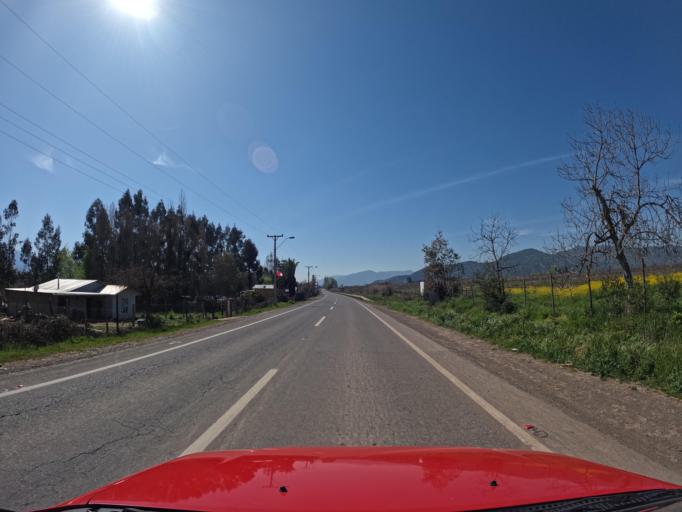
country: CL
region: Maule
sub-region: Provincia de Curico
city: Molina
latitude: -35.0549
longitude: -71.4837
